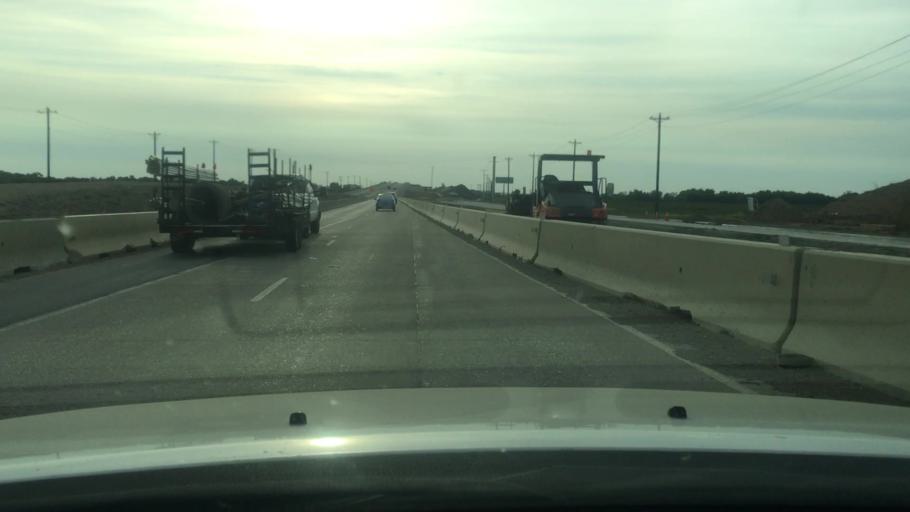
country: US
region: Texas
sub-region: Collin County
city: Prosper
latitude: 33.2189
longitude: -96.8039
